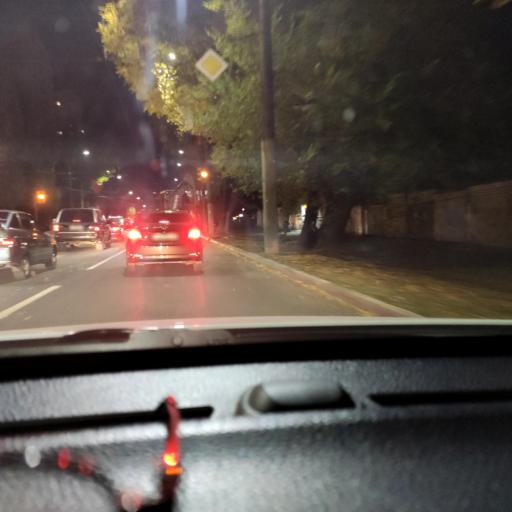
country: RU
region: Voronezj
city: Voronezh
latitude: 51.7023
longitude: 39.1741
